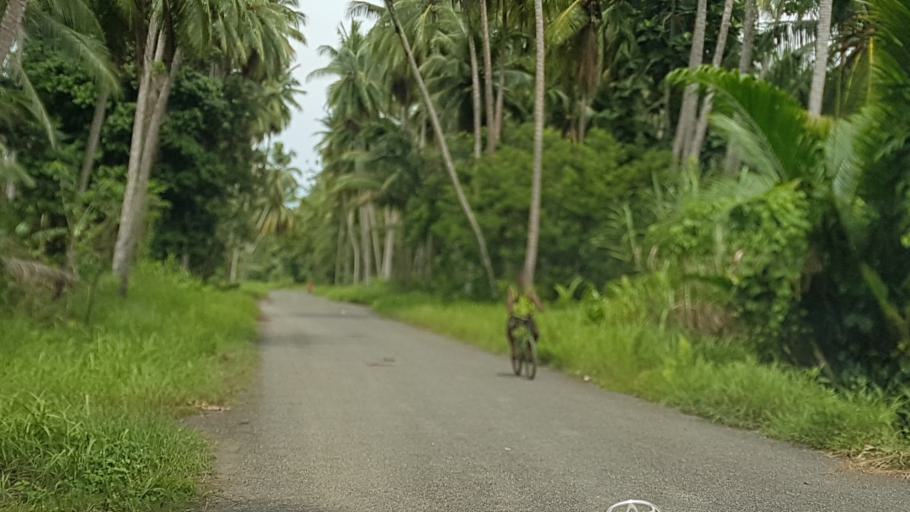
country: PG
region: Madang
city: Madang
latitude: -4.7483
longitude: 145.6619
